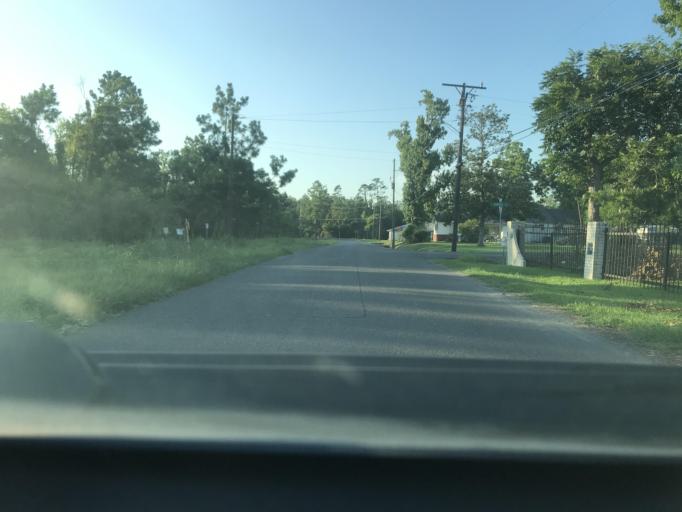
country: US
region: Louisiana
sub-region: Calcasieu Parish
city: Moss Bluff
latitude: 30.2646
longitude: -93.1843
